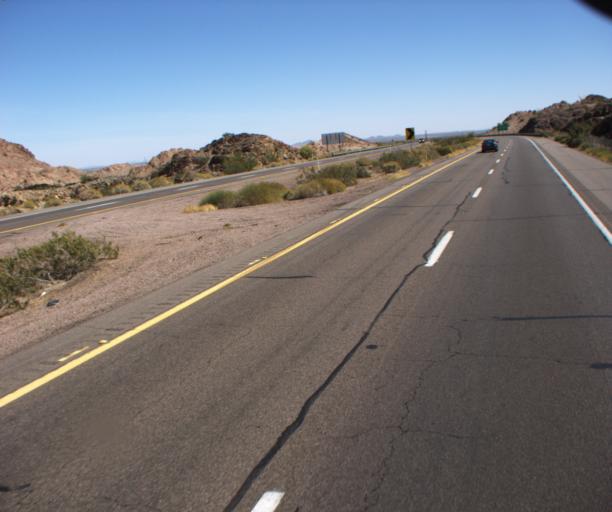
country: US
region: Arizona
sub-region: Yuma County
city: Wellton
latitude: 32.7257
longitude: -113.7472
